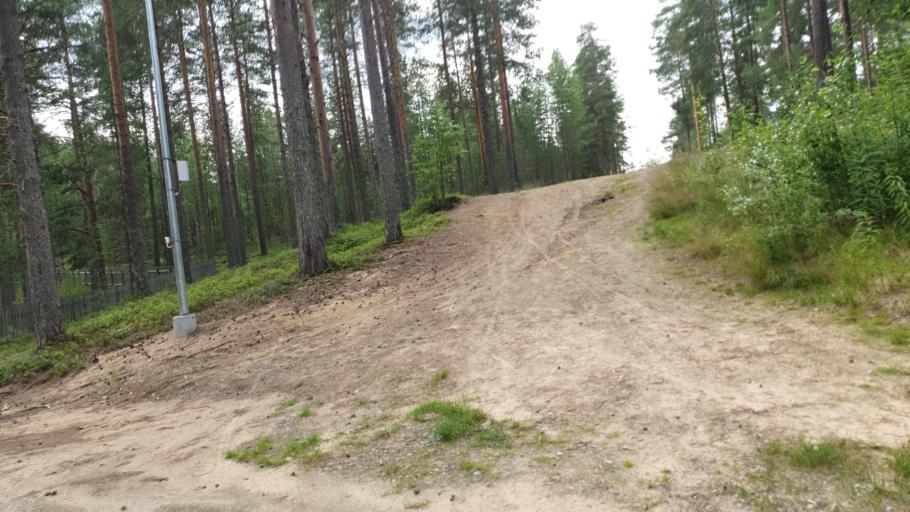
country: FI
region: Kainuu
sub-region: Kehys-Kainuu
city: Kuhmo
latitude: 64.1318
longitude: 29.5367
